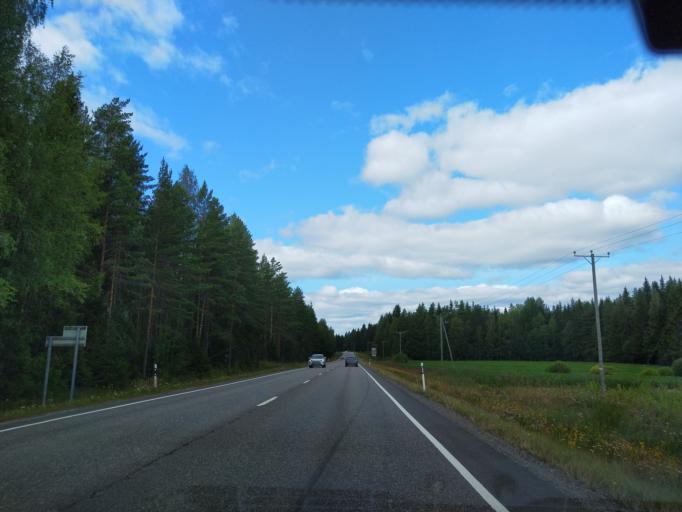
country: FI
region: Haeme
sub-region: Haemeenlinna
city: Renko
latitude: 60.7562
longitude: 24.2995
